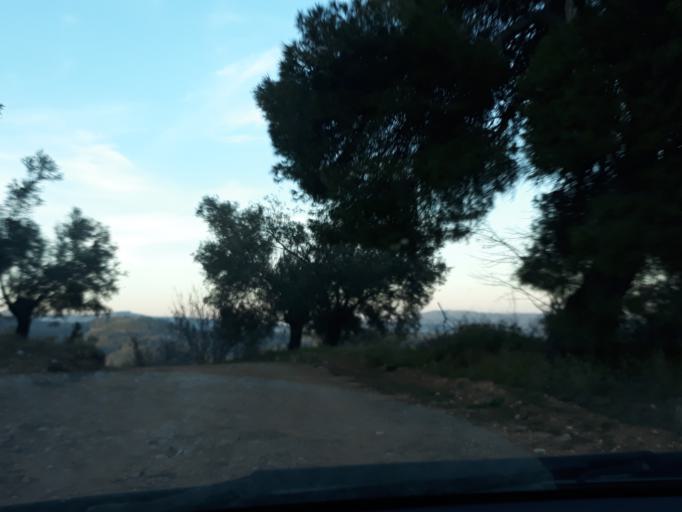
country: GR
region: Central Greece
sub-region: Nomos Voiotias
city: Asopia
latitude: 38.2771
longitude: 23.5313
